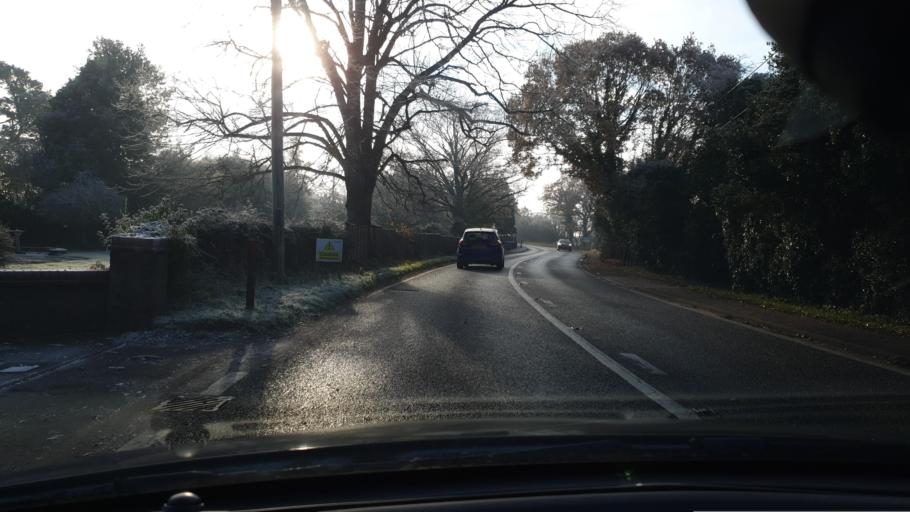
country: GB
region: England
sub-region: Essex
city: Mistley
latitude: 51.9864
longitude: 1.0974
